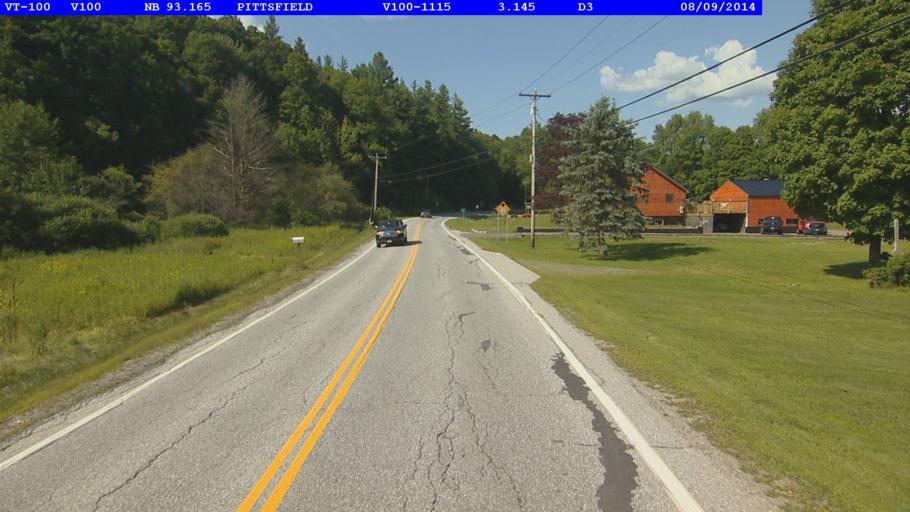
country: US
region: Vermont
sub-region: Rutland County
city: Rutland
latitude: 43.7620
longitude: -72.8185
